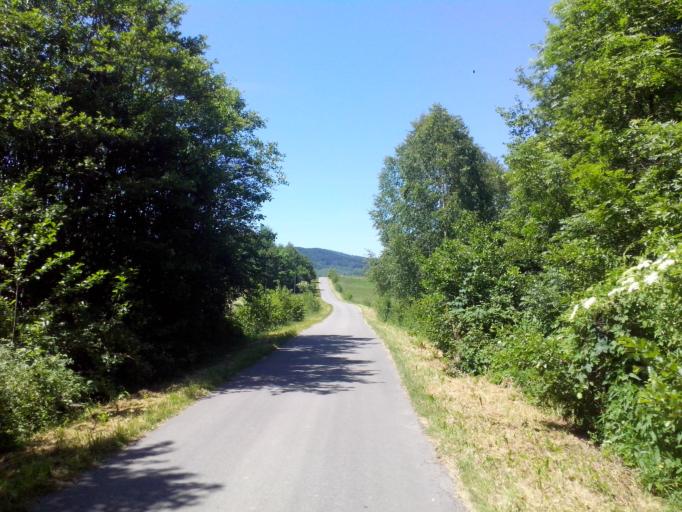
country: PL
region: Subcarpathian Voivodeship
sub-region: Powiat strzyzowski
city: Wysoka Strzyzowska
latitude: 49.8205
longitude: 21.7520
